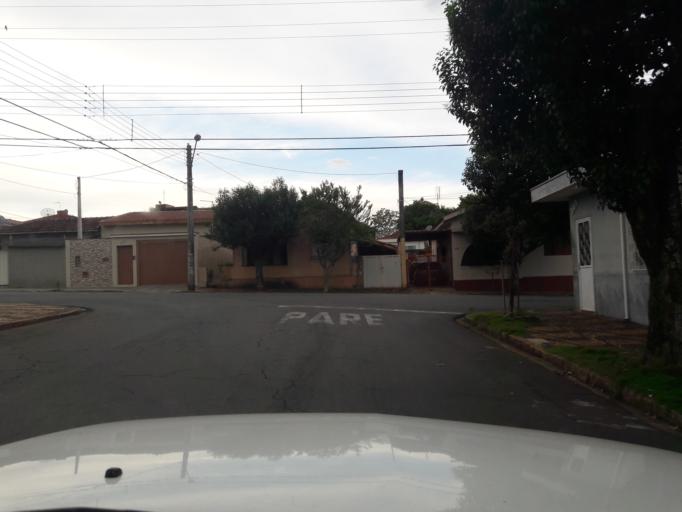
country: BR
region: Sao Paulo
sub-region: Moji-Guacu
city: Mogi-Gaucu
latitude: -22.3634
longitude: -46.9416
